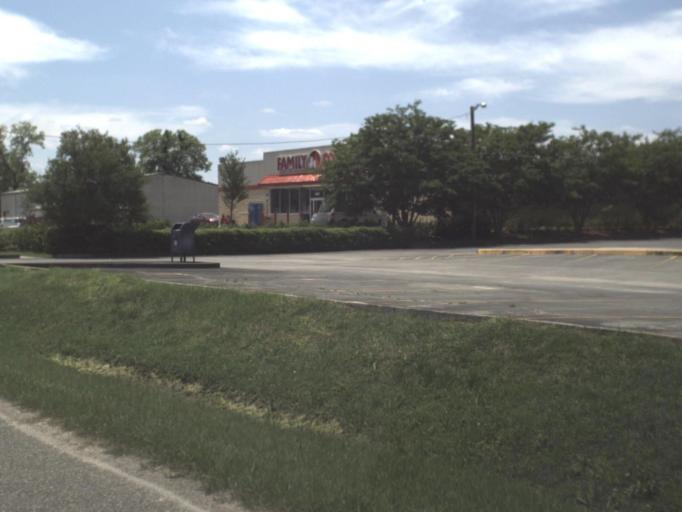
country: US
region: Florida
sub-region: Calhoun County
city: Blountstown
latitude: 30.5757
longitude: -85.1272
